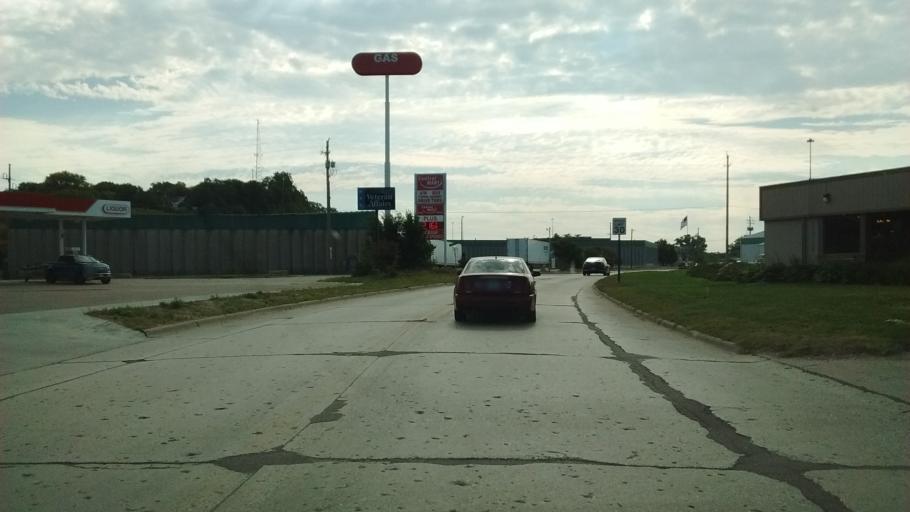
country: US
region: Nebraska
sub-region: Dakota County
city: South Sioux City
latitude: 42.4944
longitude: -96.4234
